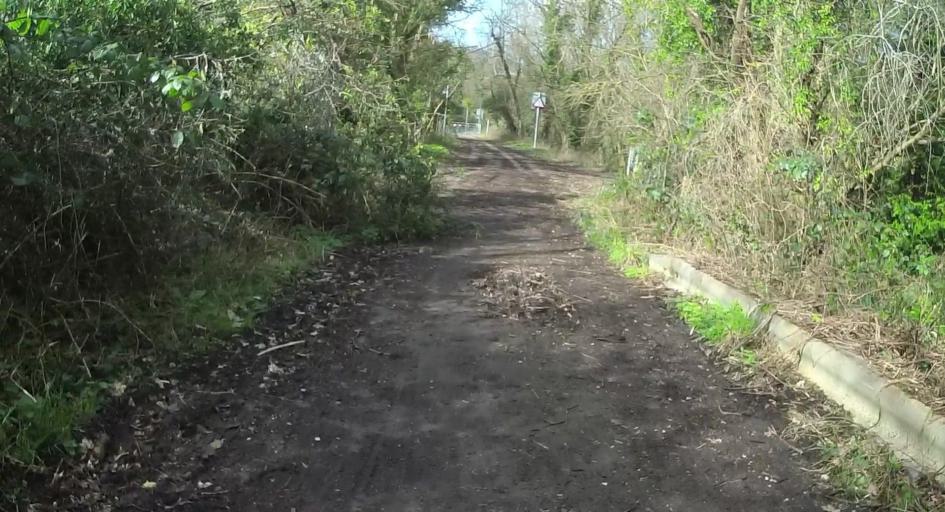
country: GB
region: England
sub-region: West Berkshire
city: Thatcham
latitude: 51.3719
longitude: -1.2535
